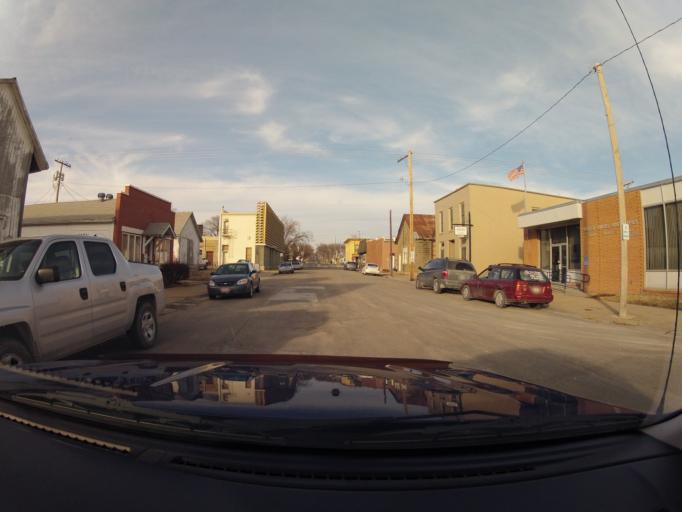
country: US
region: Kansas
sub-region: Pottawatomie County
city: Saint Marys
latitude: 39.1933
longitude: -96.0716
